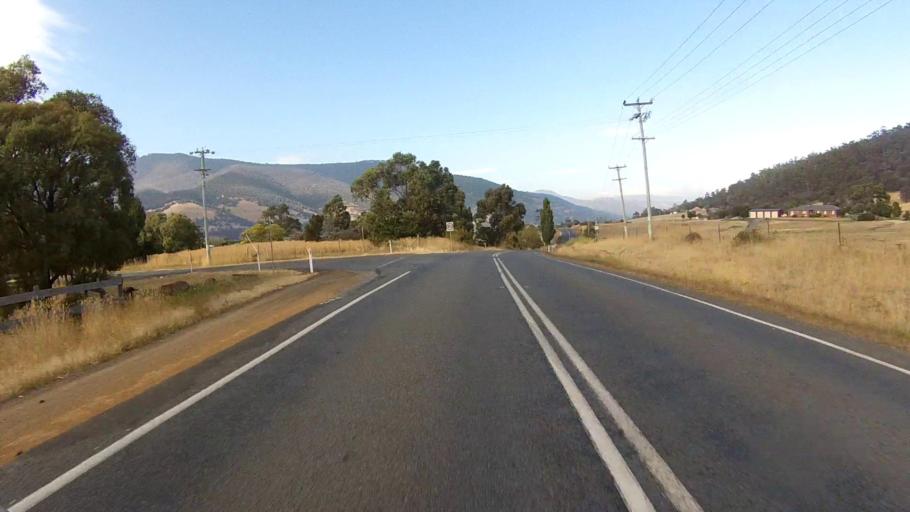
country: AU
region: Tasmania
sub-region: Brighton
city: Bridgewater
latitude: -42.7338
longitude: 147.1760
